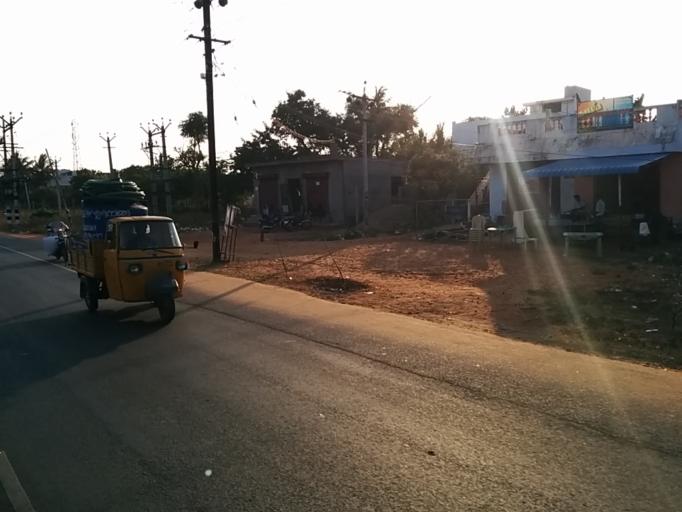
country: IN
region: Tamil Nadu
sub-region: Villupuram
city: Auroville
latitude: 11.9908
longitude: 79.8488
